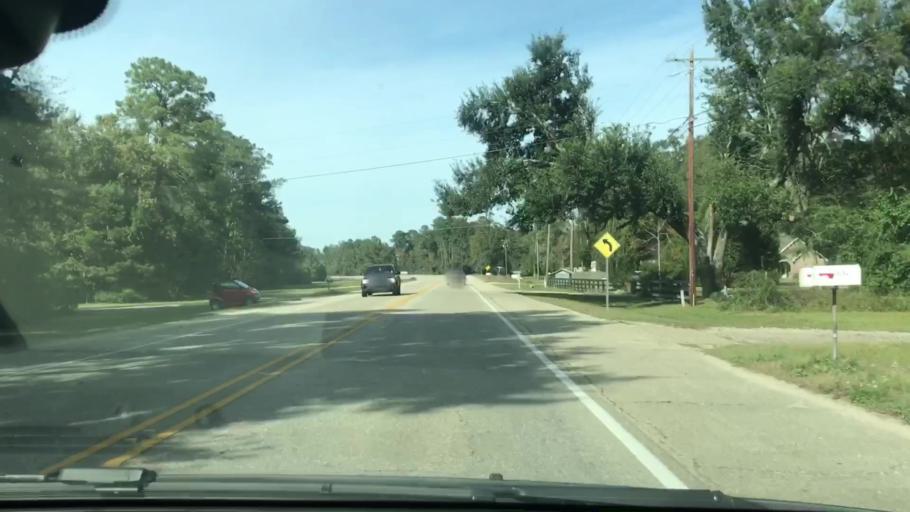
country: US
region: Louisiana
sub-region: Saint Tammany Parish
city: Pearl River
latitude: 30.4360
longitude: -89.7871
